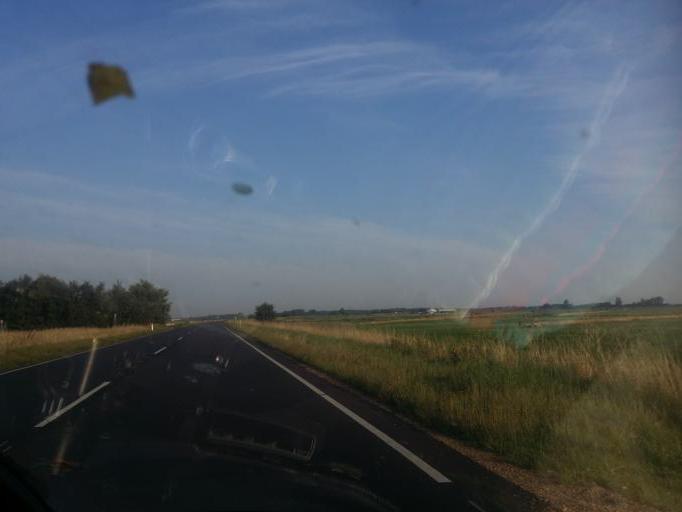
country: DK
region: South Denmark
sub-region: Tonder Kommune
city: Tonder
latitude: 54.9152
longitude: 8.8996
